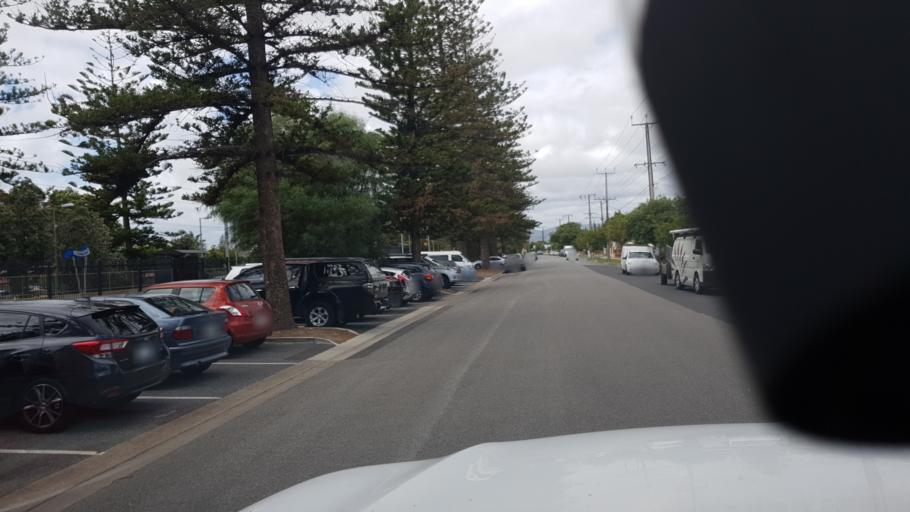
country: AU
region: South Australia
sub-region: Holdfast Bay
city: Glenelg East
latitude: -34.9800
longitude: 138.5247
